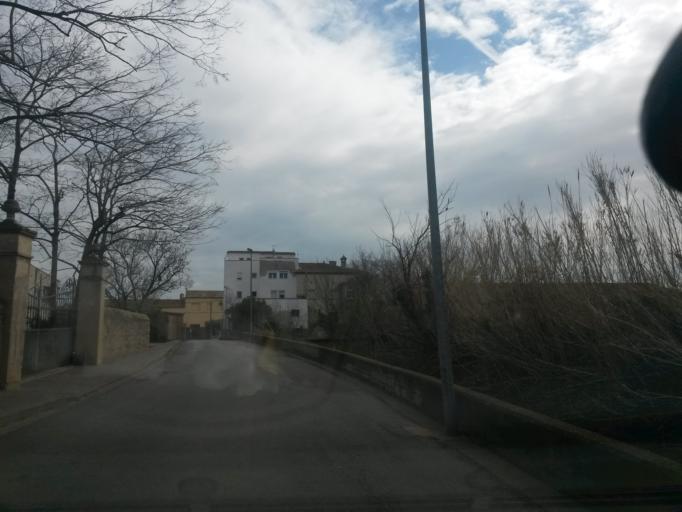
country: ES
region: Catalonia
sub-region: Provincia de Girona
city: Cabanes
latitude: 42.3088
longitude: 2.9744
